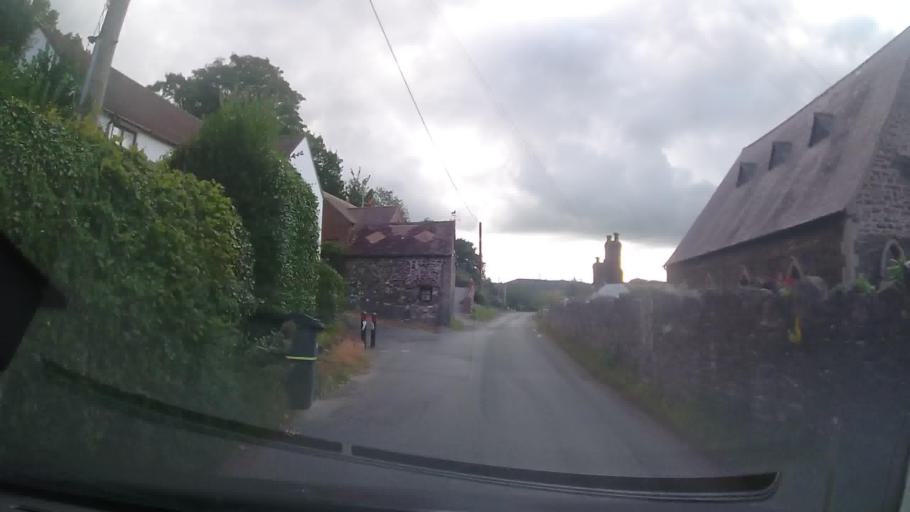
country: GB
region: England
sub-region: Shropshire
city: Pontesbury
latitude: 52.6120
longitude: -2.9291
